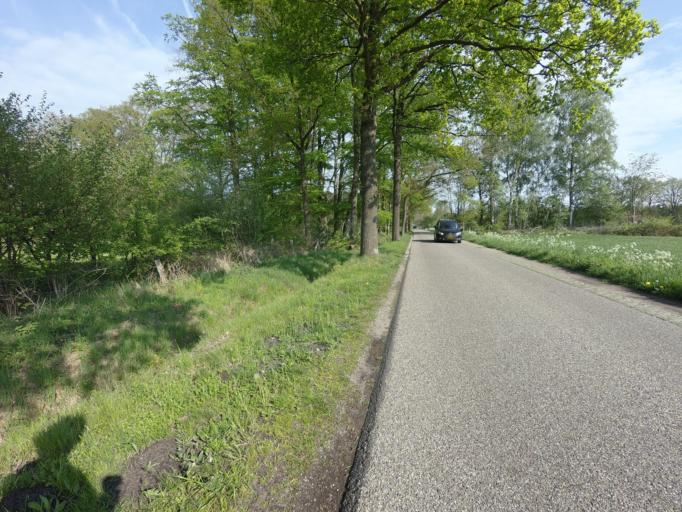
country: NL
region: Overijssel
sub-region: Gemeente Haaksbergen
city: Haaksbergen
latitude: 52.1736
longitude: 6.8146
